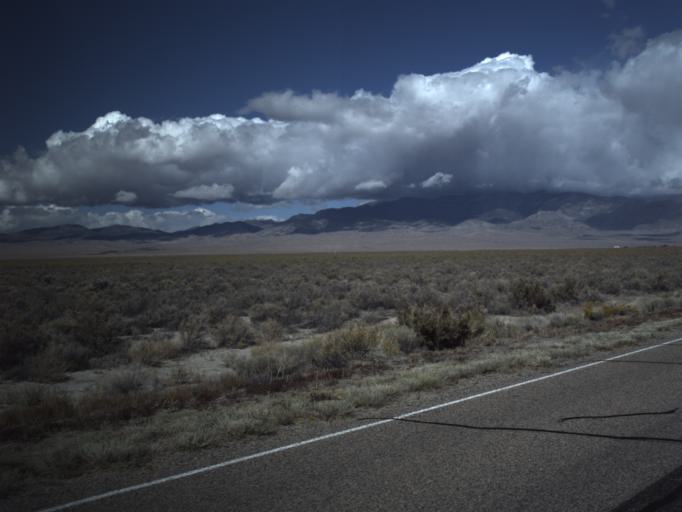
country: US
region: Nevada
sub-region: White Pine County
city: McGill
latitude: 39.0260
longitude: -114.0356
